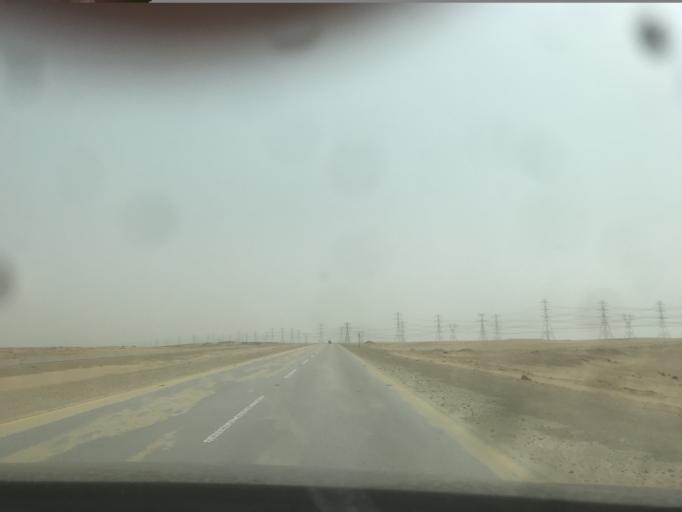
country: SA
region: Eastern Province
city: Abqaiq
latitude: 25.9182
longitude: 49.7870
